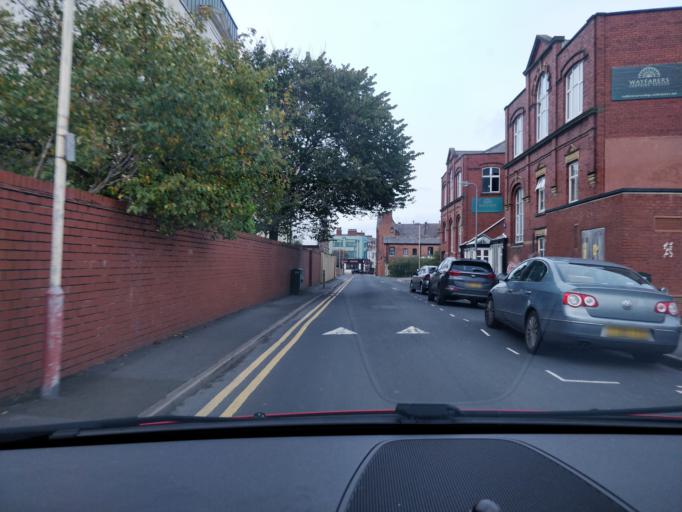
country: GB
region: England
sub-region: Sefton
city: Southport
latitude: 53.6486
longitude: -3.0076
